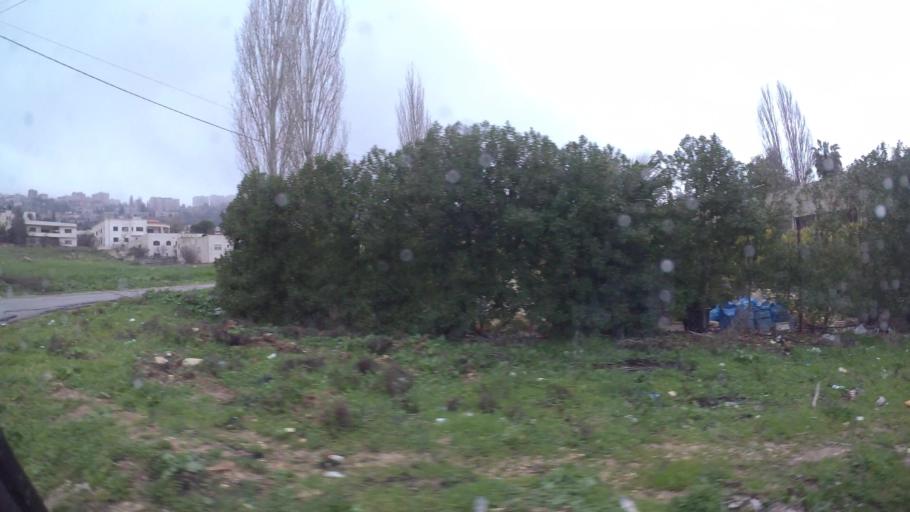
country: JO
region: Amman
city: Al Jubayhah
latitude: 32.0364
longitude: 35.8343
